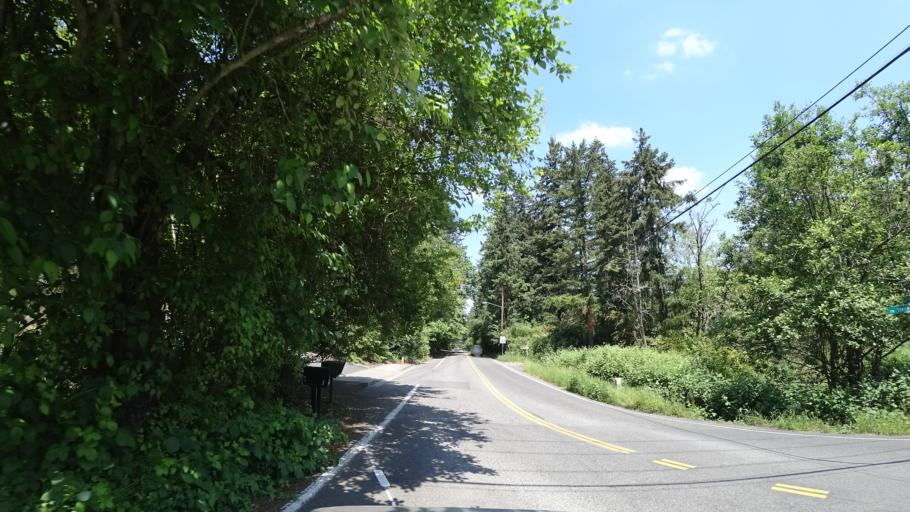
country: US
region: Oregon
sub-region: Clackamas County
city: Lake Oswego
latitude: 45.4403
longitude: -122.7128
